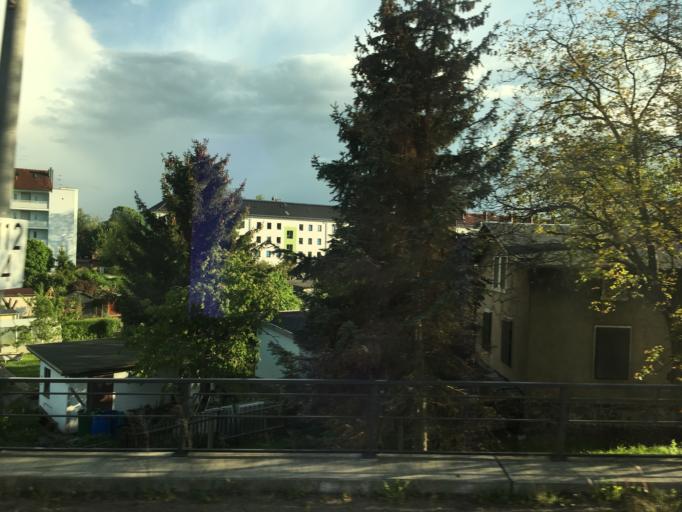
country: DE
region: Saxony
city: Dresden
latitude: 51.0867
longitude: 13.7165
